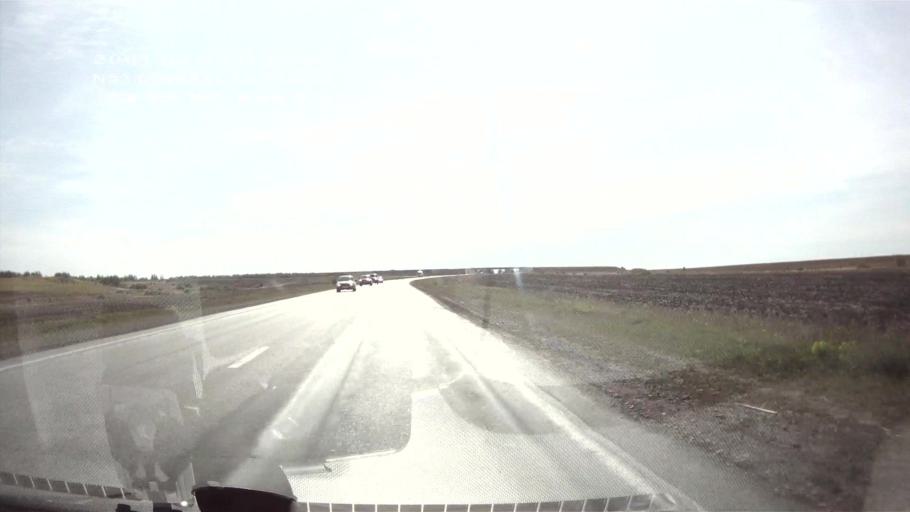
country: RU
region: Samara
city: Syzran'
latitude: 53.0082
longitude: 48.3324
